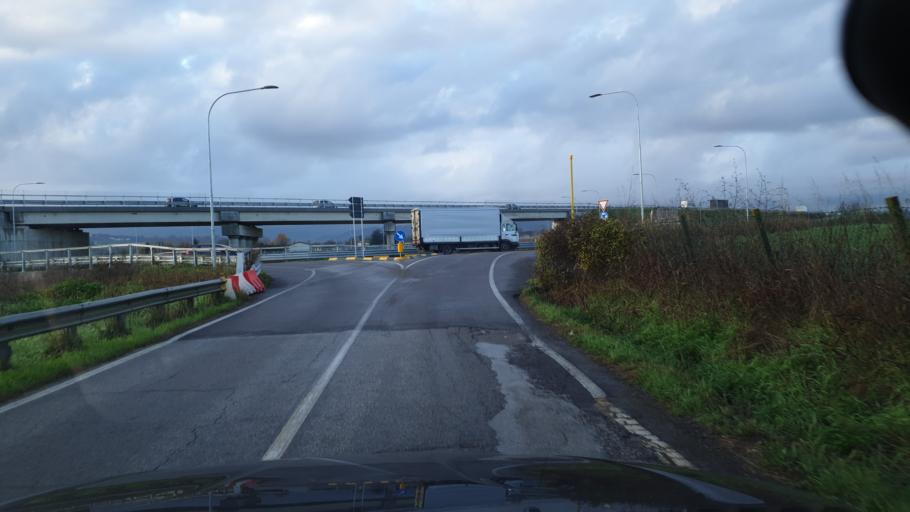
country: IT
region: Emilia-Romagna
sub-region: Provincia di Bologna
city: Crespellano
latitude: 44.5175
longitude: 11.1145
